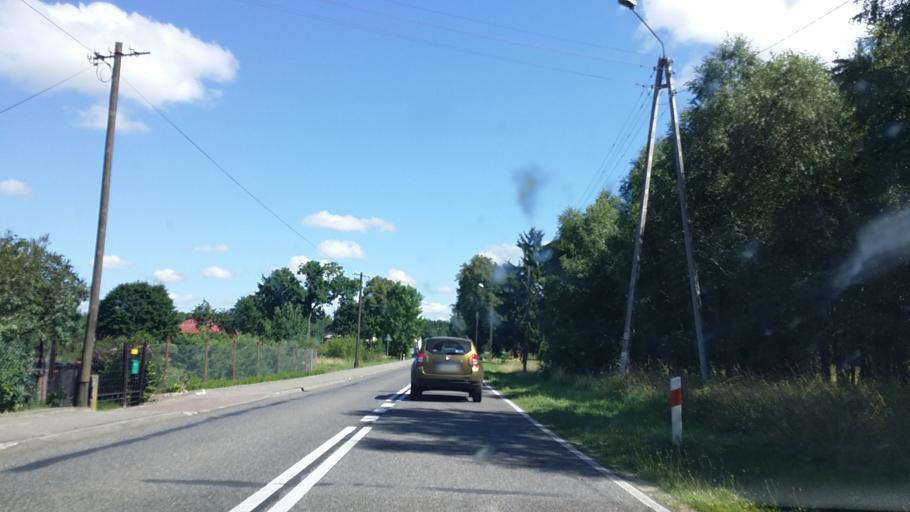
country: PL
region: West Pomeranian Voivodeship
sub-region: Powiat drawski
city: Drawsko Pomorskie
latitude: 53.4379
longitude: 15.8233
